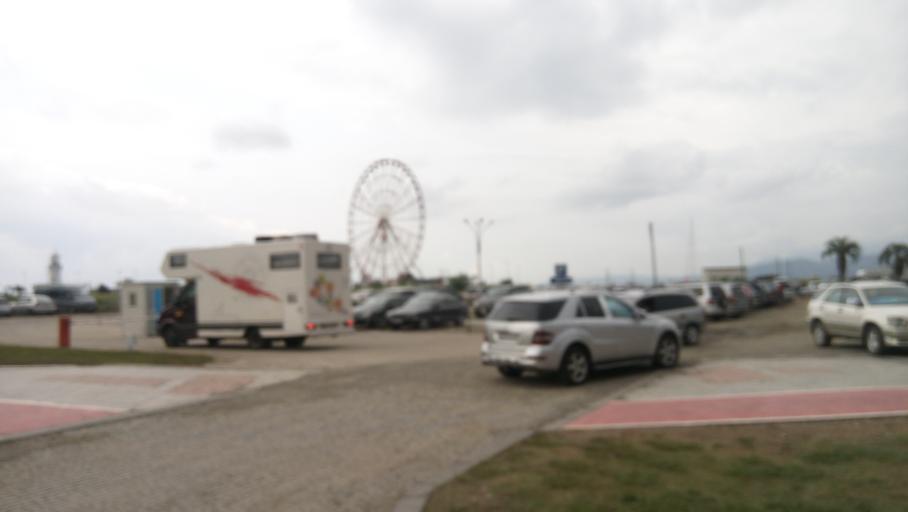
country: GE
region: Ajaria
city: Batumi
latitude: 41.6527
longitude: 41.6413
